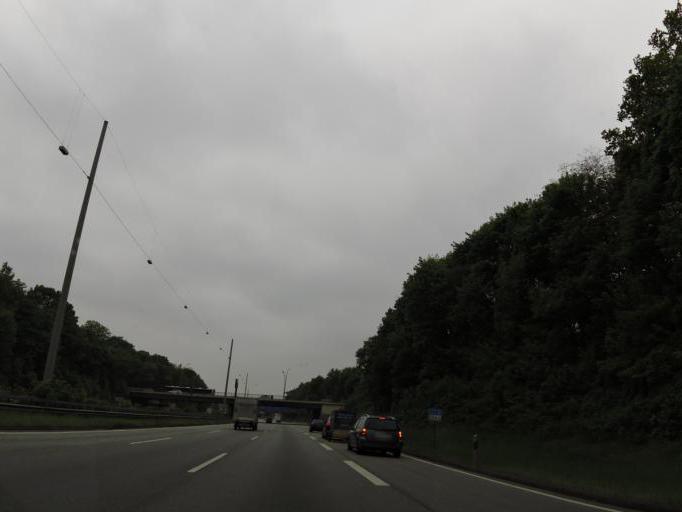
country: DE
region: Hamburg
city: Stellingen
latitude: 53.5710
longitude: 9.9023
